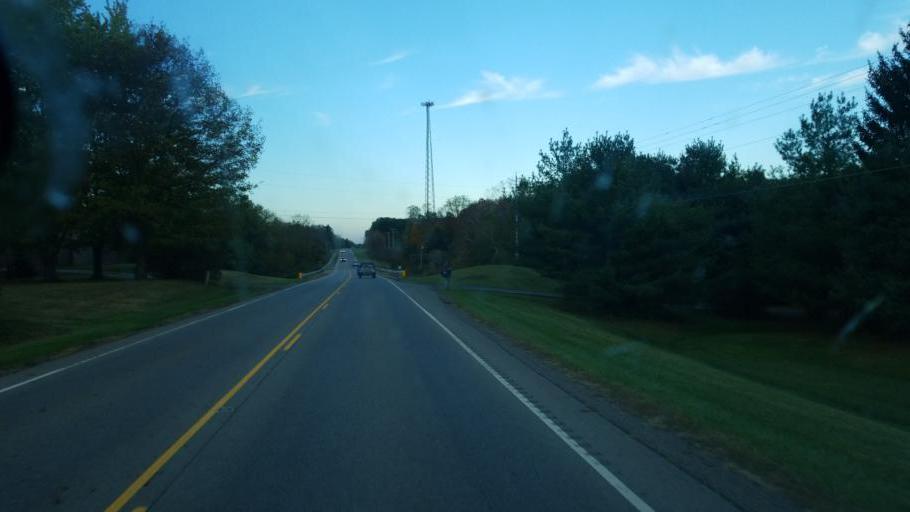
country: US
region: Ohio
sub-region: Licking County
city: Johnstown
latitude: 40.2004
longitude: -82.5840
